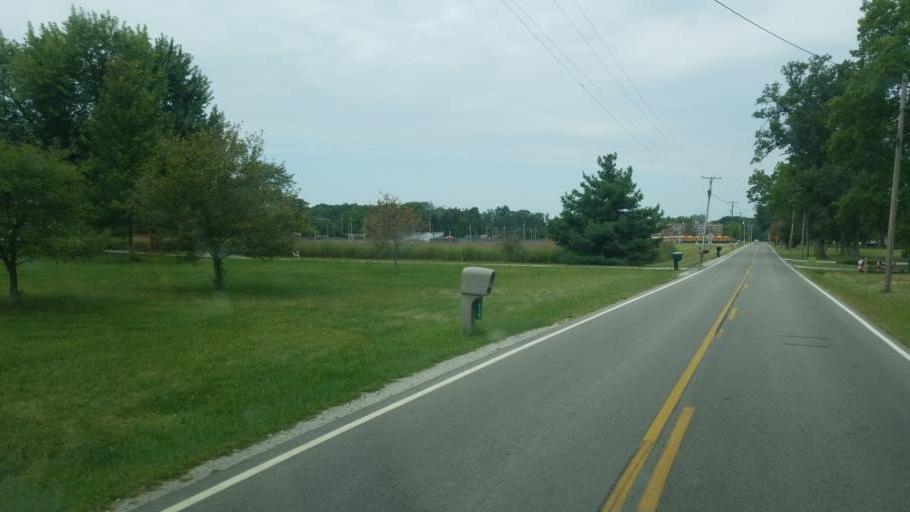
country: US
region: Ohio
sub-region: Marion County
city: Marion
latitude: 40.5172
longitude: -83.1320
